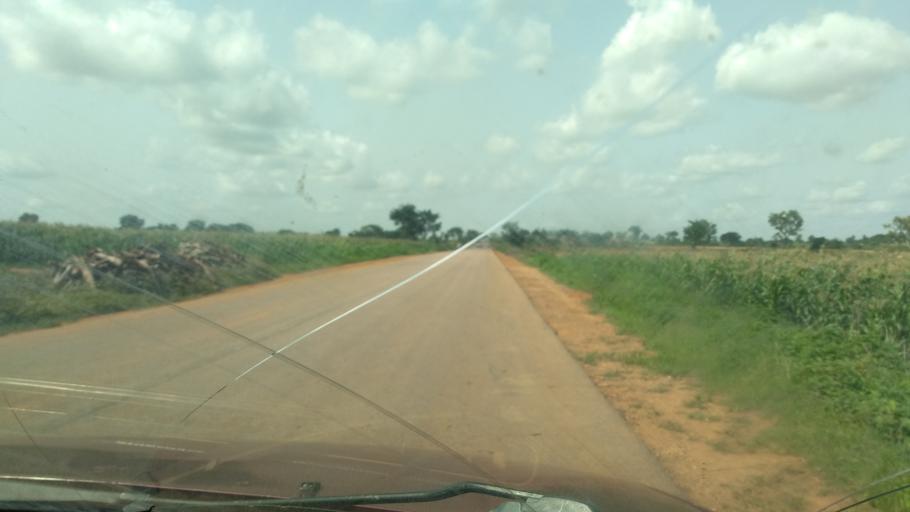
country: NG
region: Katsina
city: Sabuwa
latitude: 11.0494
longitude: 7.1575
